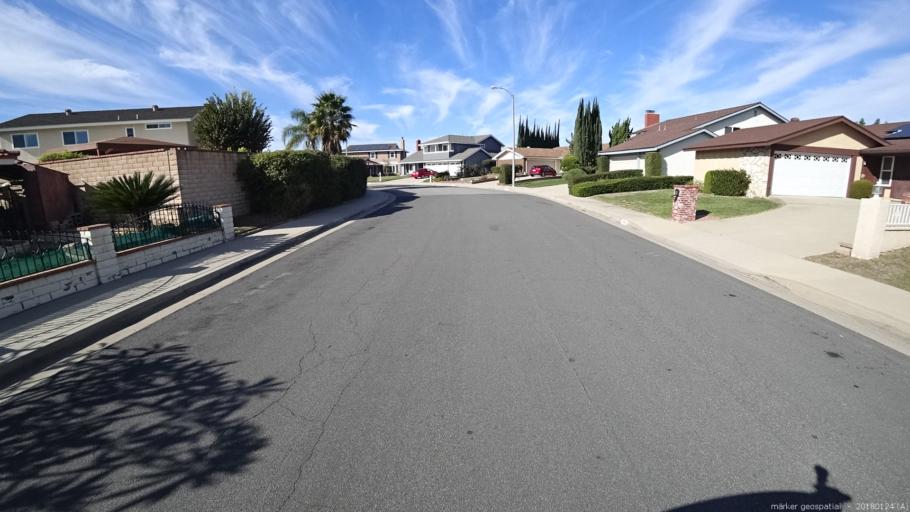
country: US
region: California
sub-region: Los Angeles County
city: Diamond Bar
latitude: 34.0138
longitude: -117.8084
